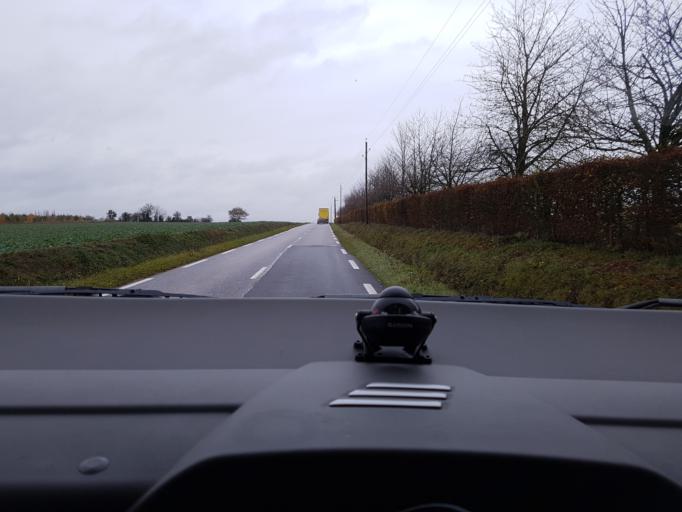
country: FR
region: Haute-Normandie
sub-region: Departement de l'Eure
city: Etrepagny
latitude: 49.3934
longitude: 1.6043
